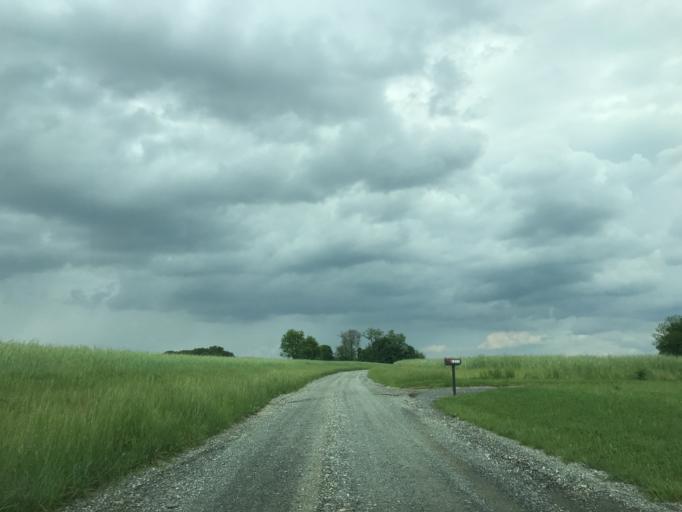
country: US
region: Pennsylvania
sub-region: York County
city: Susquehanna Trails
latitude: 39.6971
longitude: -76.3544
